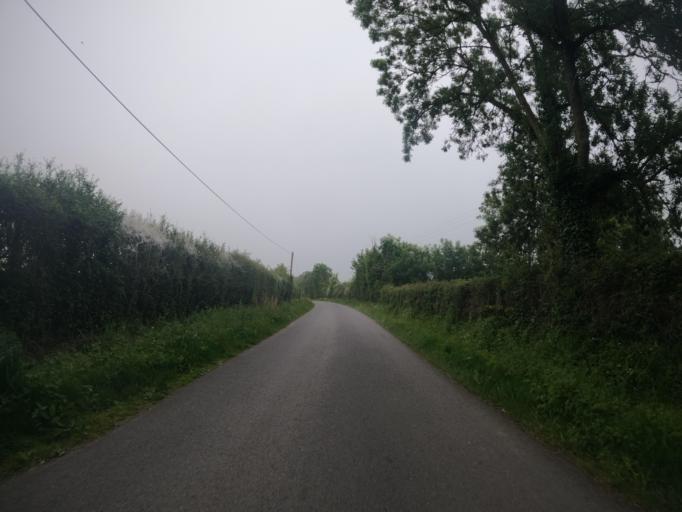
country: FR
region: Poitou-Charentes
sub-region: Departement des Deux-Sevres
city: Chiche
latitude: 46.8665
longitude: -0.3385
